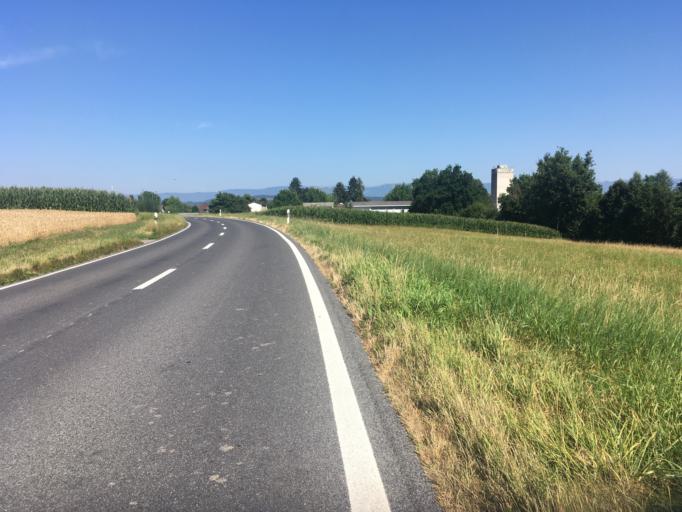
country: CH
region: Bern
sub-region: Bern-Mittelland District
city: Fraubrunnen
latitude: 47.0815
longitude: 7.5292
